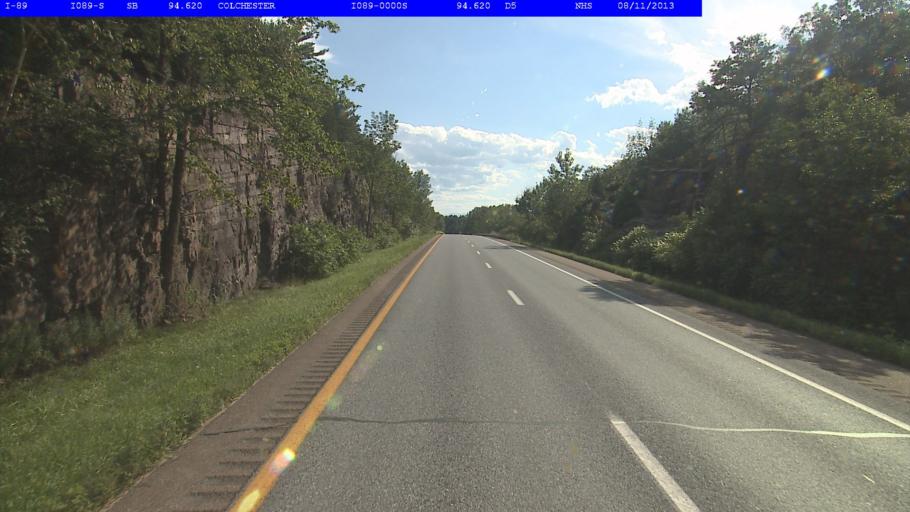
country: US
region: Vermont
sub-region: Chittenden County
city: Colchester
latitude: 44.5461
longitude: -73.1931
